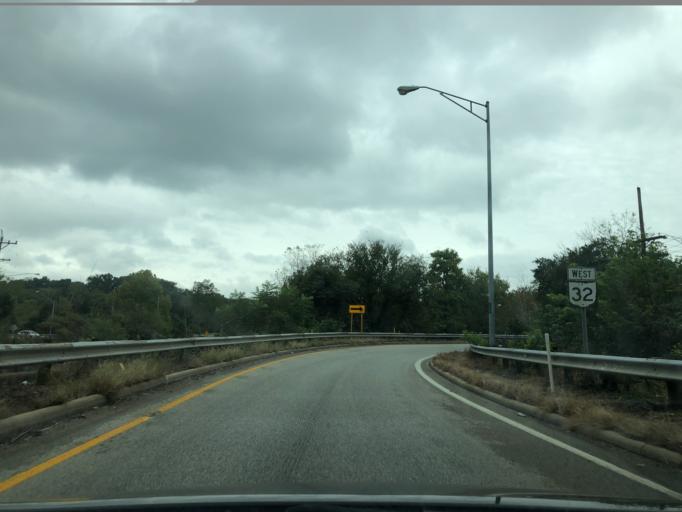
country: US
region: Ohio
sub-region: Hamilton County
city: Turpin Hills
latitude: 39.1090
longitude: -84.3998
